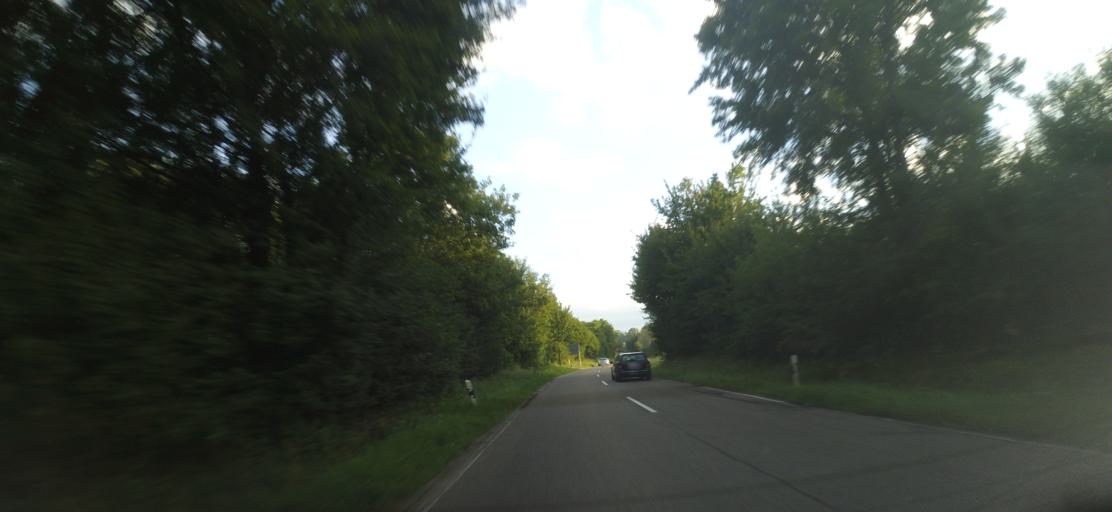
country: DE
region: Saarland
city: Sankt Ingbert
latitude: 49.1964
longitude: 7.1315
